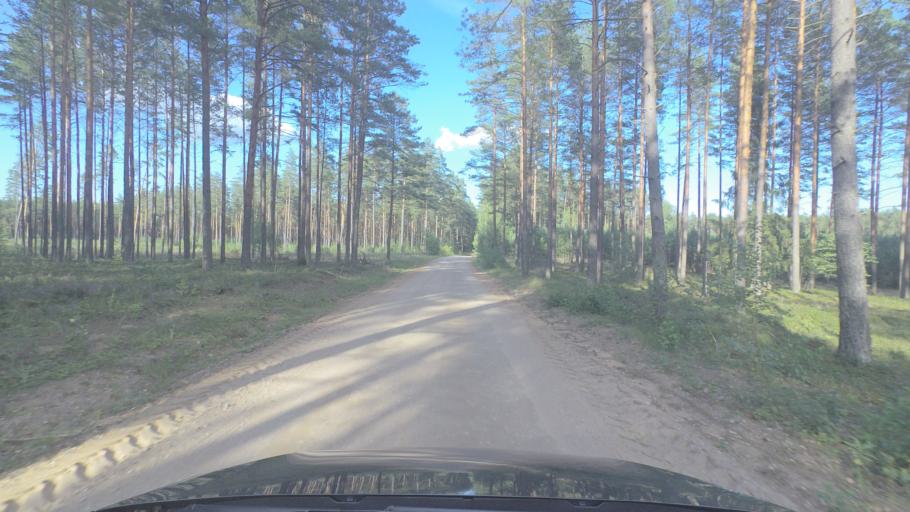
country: LT
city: Pabrade
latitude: 55.1607
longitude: 25.8129
